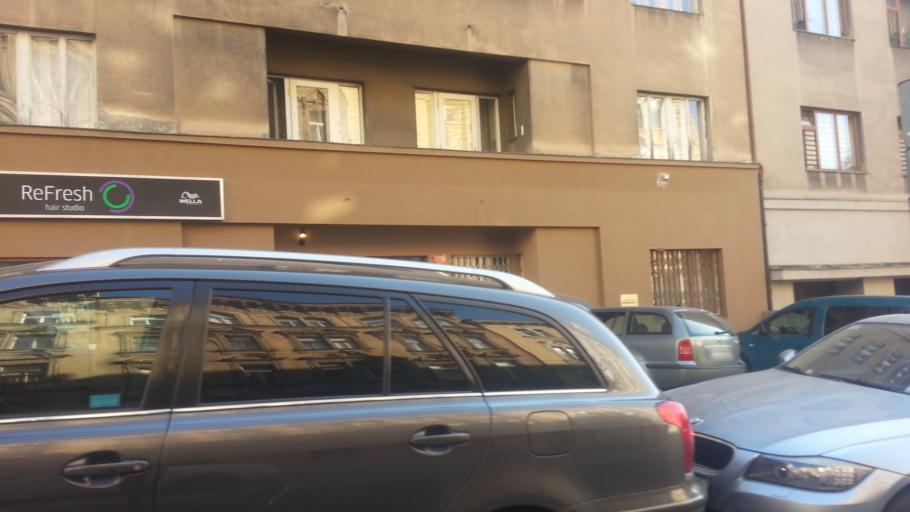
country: CZ
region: Praha
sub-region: Praha 8
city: Karlin
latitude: 50.0751
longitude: 14.4545
